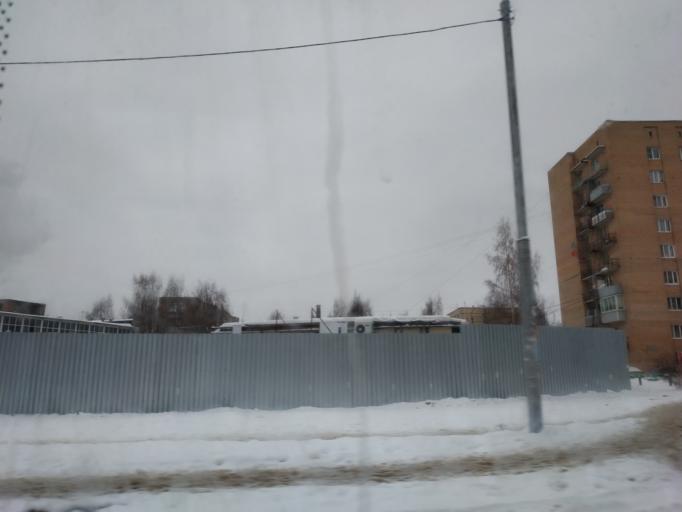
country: RU
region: Moskovskaya
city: Shchelkovo
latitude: 55.9302
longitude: 37.9887
